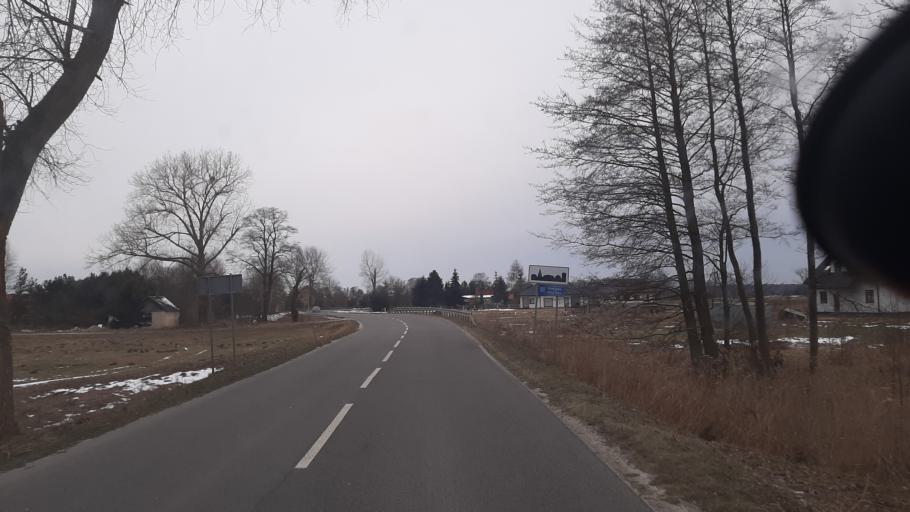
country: PL
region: Lublin Voivodeship
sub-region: Powiat lubartowski
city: Kamionka
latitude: 51.4878
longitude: 22.4434
